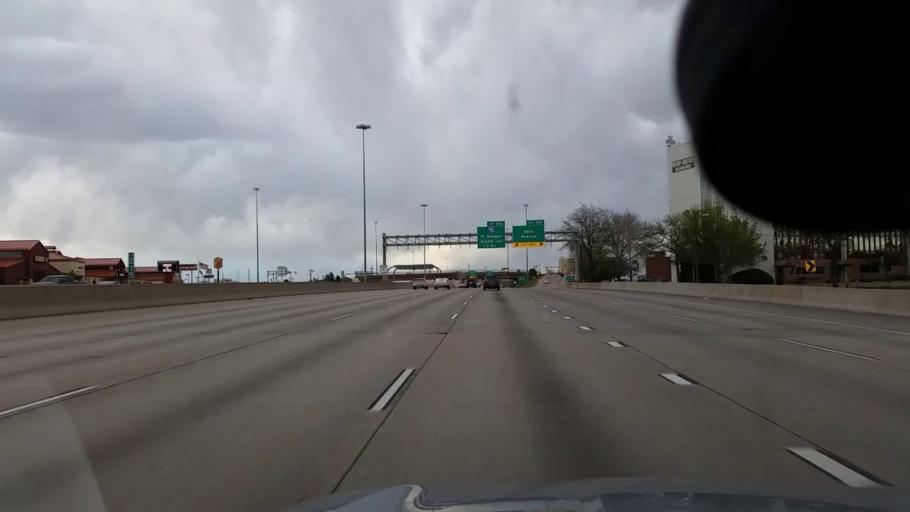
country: US
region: Colorado
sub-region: Adams County
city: Twin Lakes
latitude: 39.7981
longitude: -104.9863
